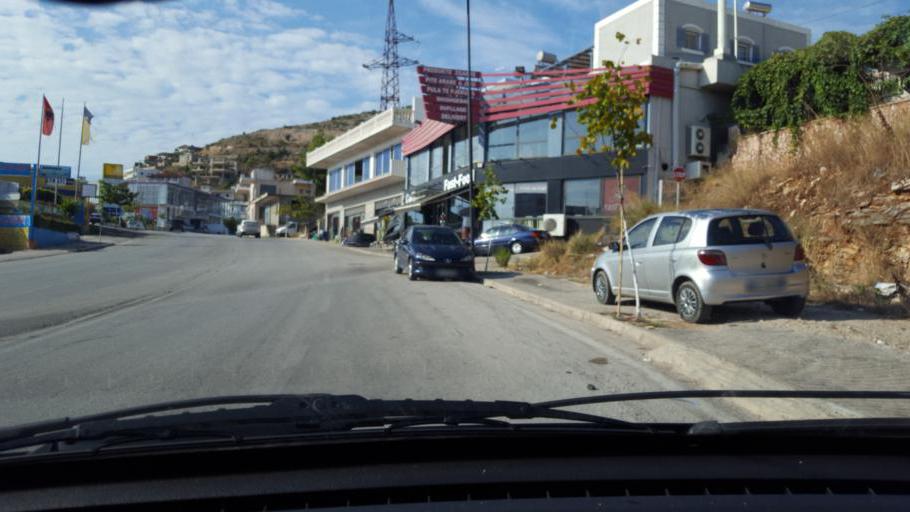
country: AL
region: Vlore
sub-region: Rrethi i Sarandes
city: Sarande
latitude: 39.8709
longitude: 20.0277
